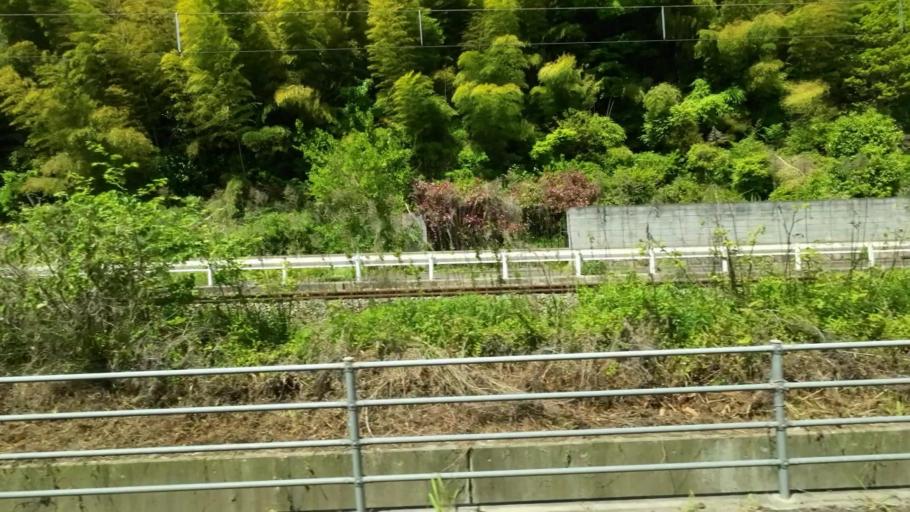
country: JP
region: Ehime
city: Hojo
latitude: 34.0779
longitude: 132.9853
